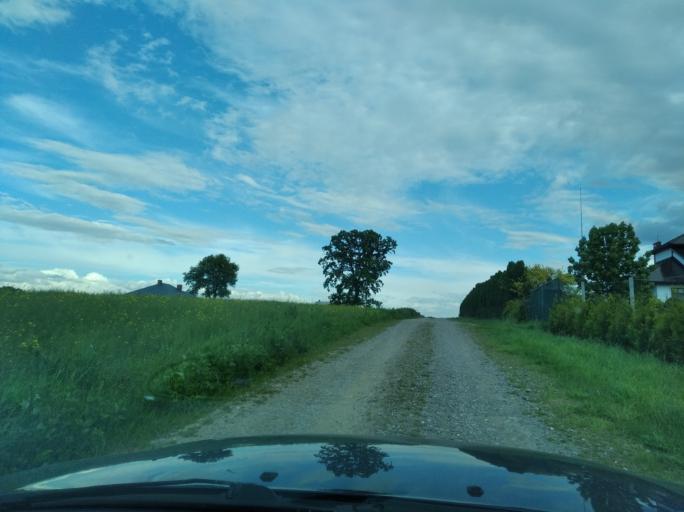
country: PL
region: Subcarpathian Voivodeship
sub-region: Powiat jaroslawski
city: Pawlosiow
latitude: 49.9697
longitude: 22.6206
